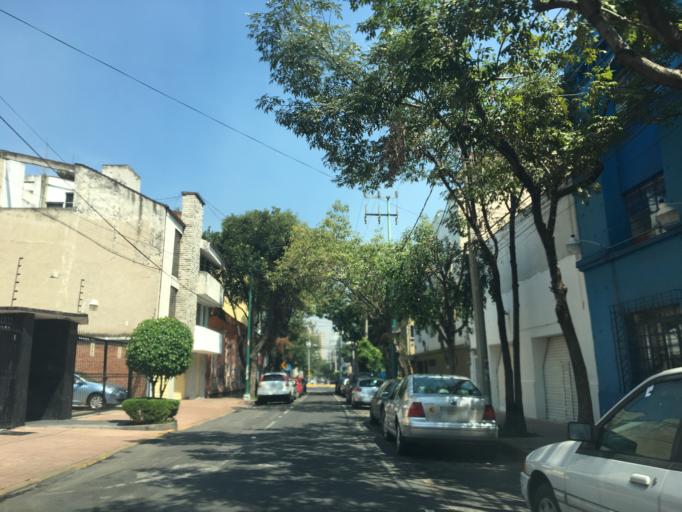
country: MX
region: Mexico City
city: Polanco
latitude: 19.4064
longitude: -99.1828
